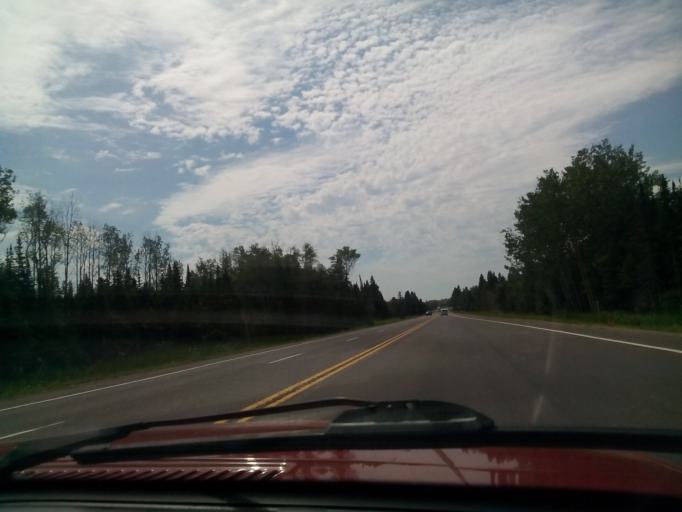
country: US
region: Michigan
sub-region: Schoolcraft County
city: Manistique
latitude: 46.0048
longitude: -85.9995
